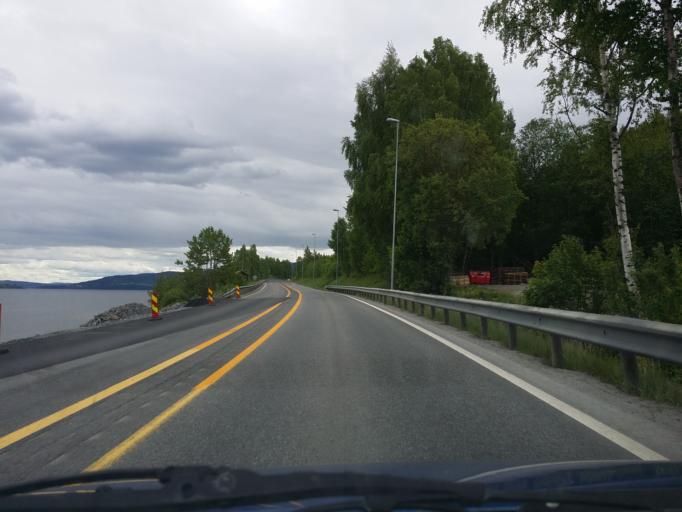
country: NO
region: Oppland
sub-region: Lillehammer
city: Lillehammer
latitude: 61.0429
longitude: 10.4348
